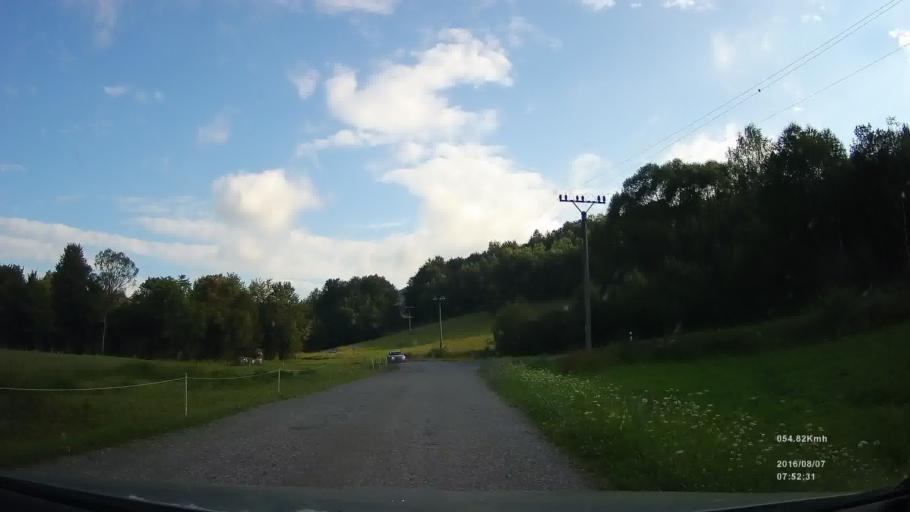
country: SK
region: Presovsky
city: Medzilaborce
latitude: 49.3091
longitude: 21.7979
